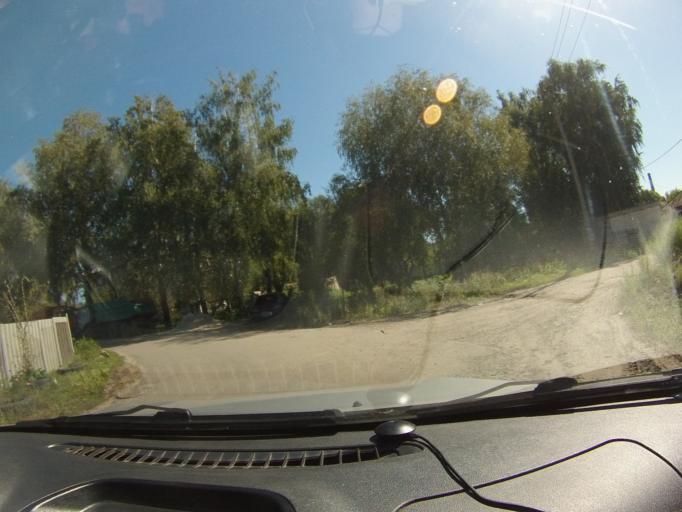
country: RU
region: Tambov
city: Donskoye
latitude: 52.7608
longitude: 41.4696
